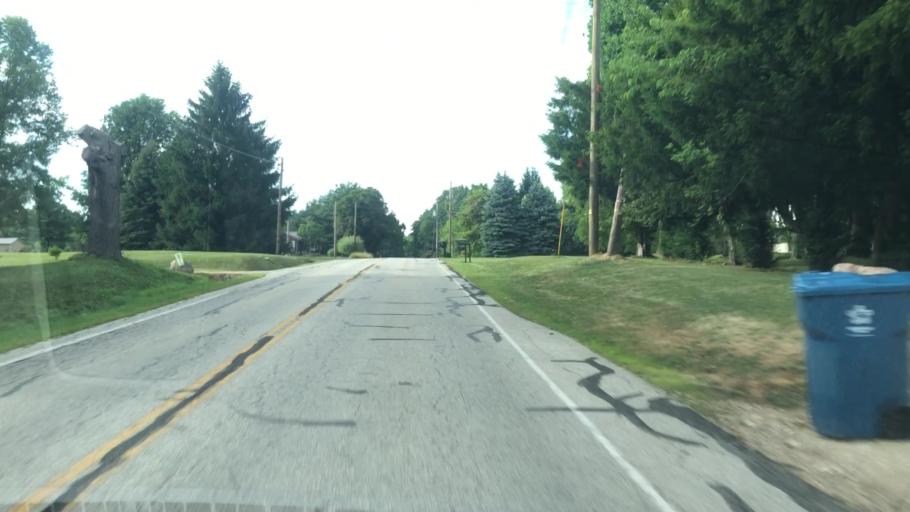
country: US
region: Ohio
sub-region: Summit County
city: Montrose-Ghent
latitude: 41.0970
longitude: -81.6874
